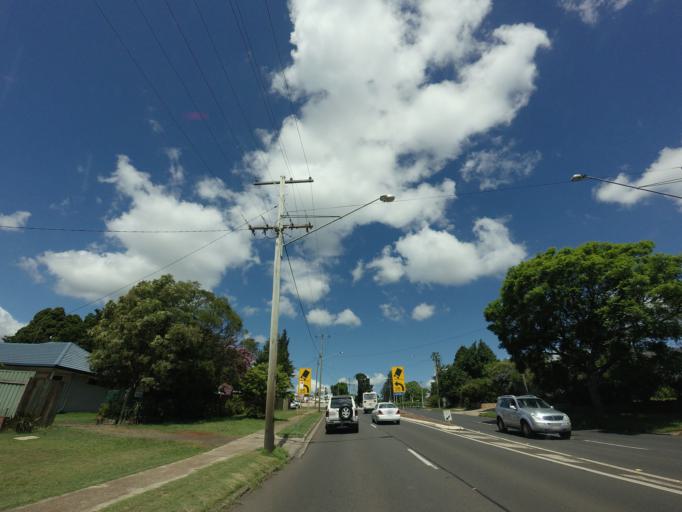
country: AU
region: Queensland
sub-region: Toowoomba
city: East Toowoomba
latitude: -27.5715
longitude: 151.9735
